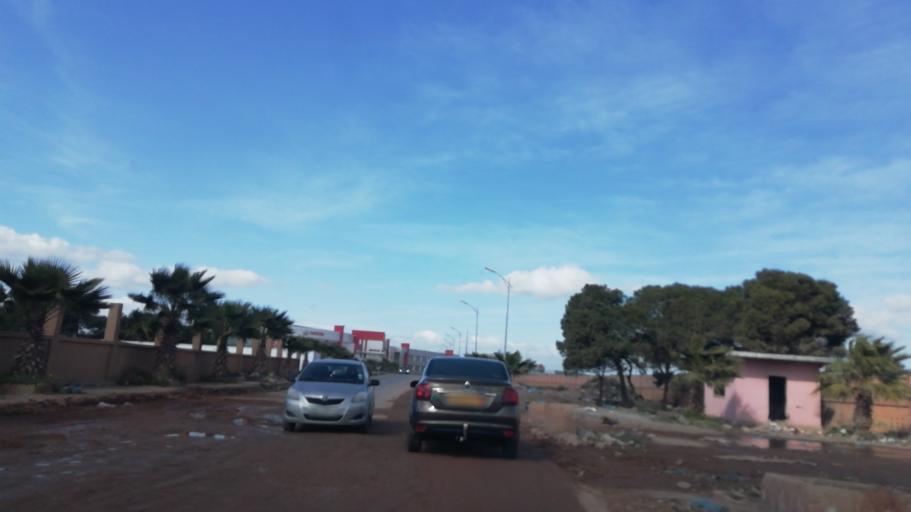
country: DZ
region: Oran
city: Es Senia
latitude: 35.6357
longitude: -0.5854
